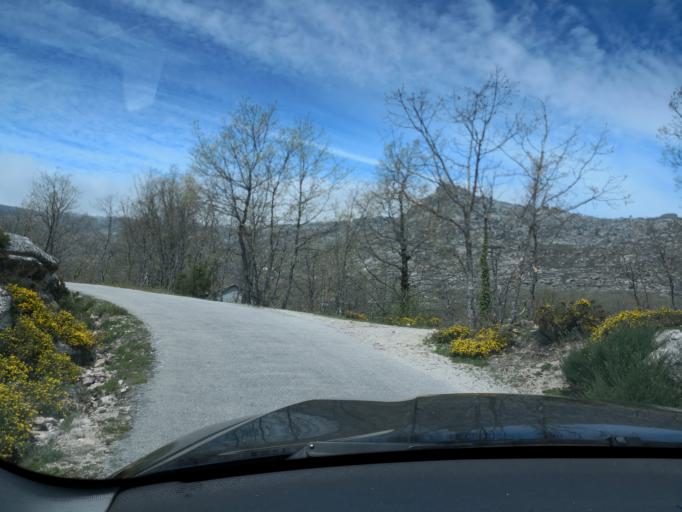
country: PT
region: Vila Real
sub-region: Vila Real
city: Vila Real
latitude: 41.3336
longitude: -7.8003
